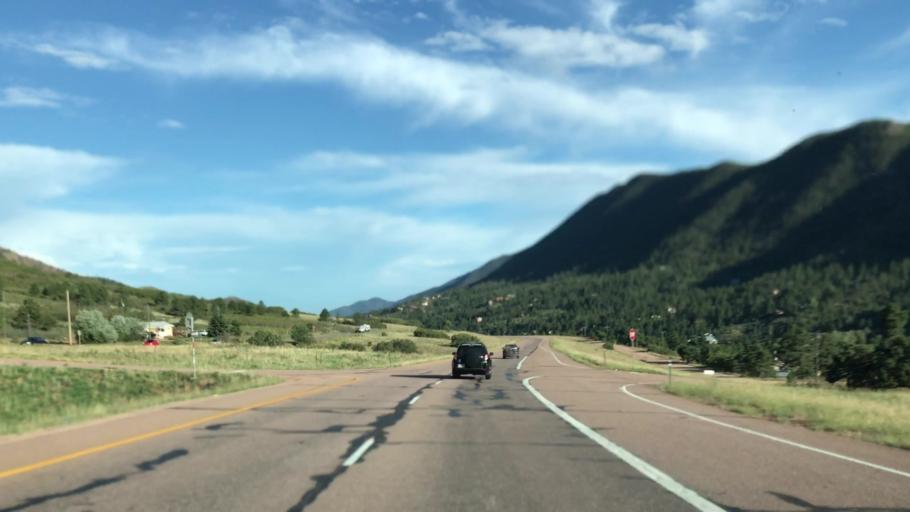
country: US
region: Colorado
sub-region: El Paso County
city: Cascade-Chipita Park
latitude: 38.9303
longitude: -105.0003
